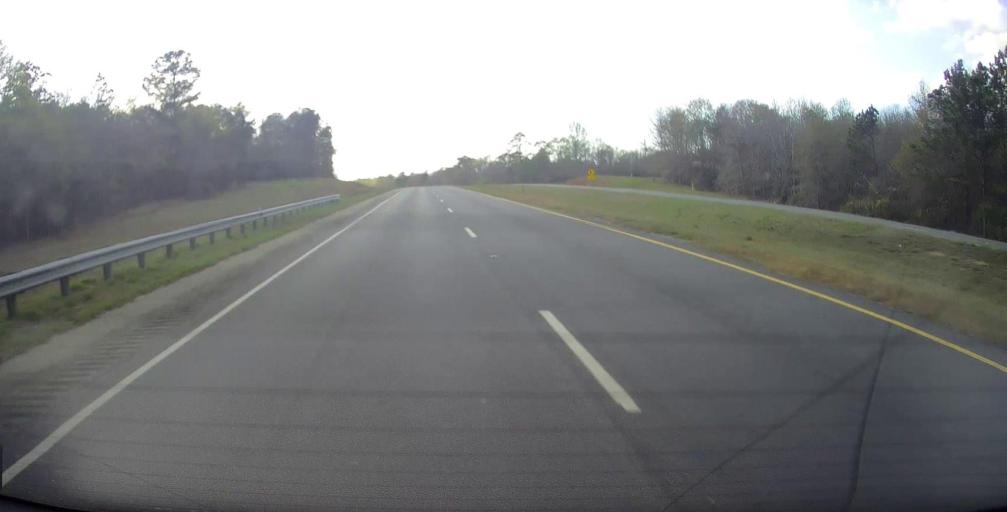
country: US
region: Georgia
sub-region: Telfair County
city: Helena
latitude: 32.1050
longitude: -82.9730
